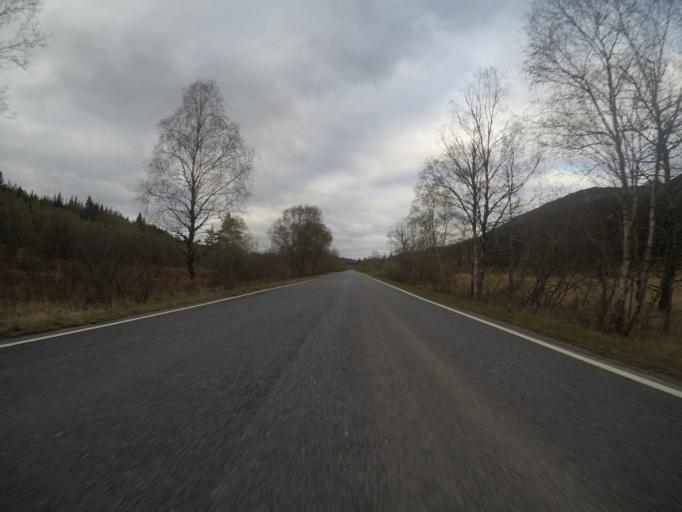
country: GB
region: Scotland
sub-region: Highland
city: Kingussie
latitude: 56.9856
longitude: -4.3459
